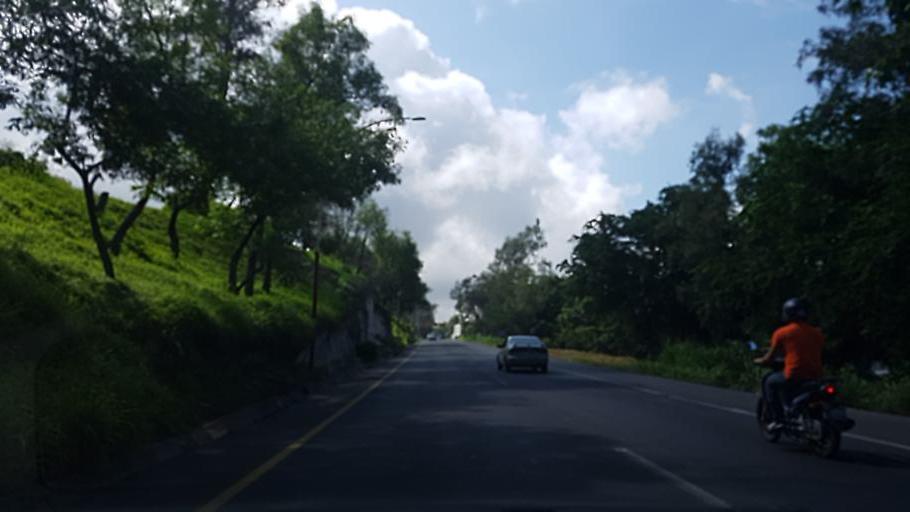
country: MX
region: Nayarit
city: Tepic
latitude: 21.4928
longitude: -104.9049
